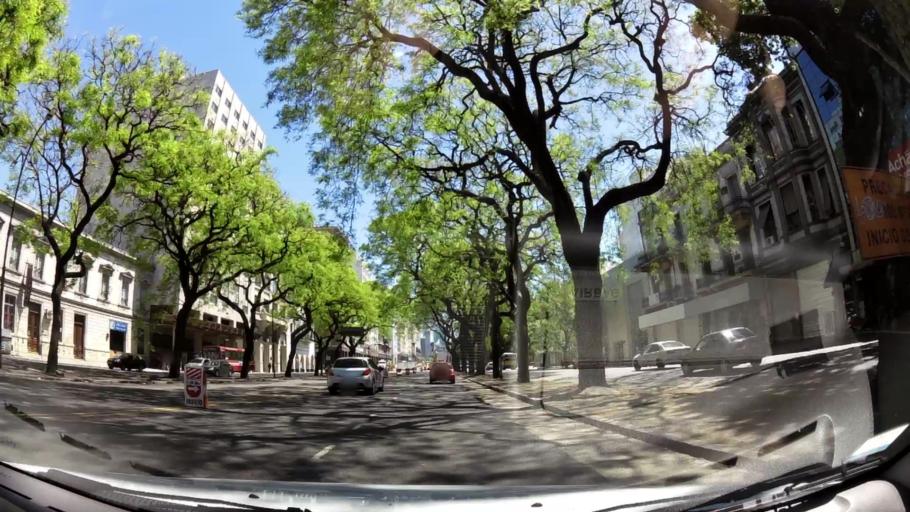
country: AR
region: Buenos Aires F.D.
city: Buenos Aires
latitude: -34.6133
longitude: -58.3692
